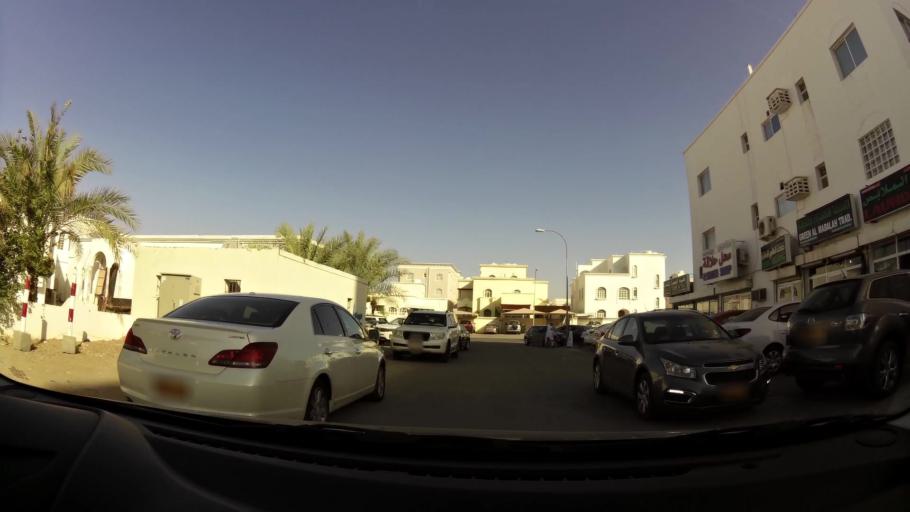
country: OM
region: Muhafazat Masqat
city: As Sib al Jadidah
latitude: 23.5986
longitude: 58.2111
